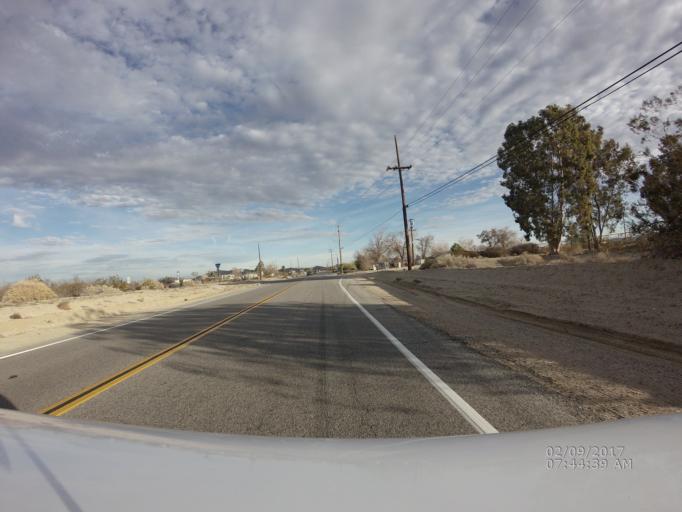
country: US
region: California
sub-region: Los Angeles County
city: Lake Los Angeles
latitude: 34.5420
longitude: -117.8356
